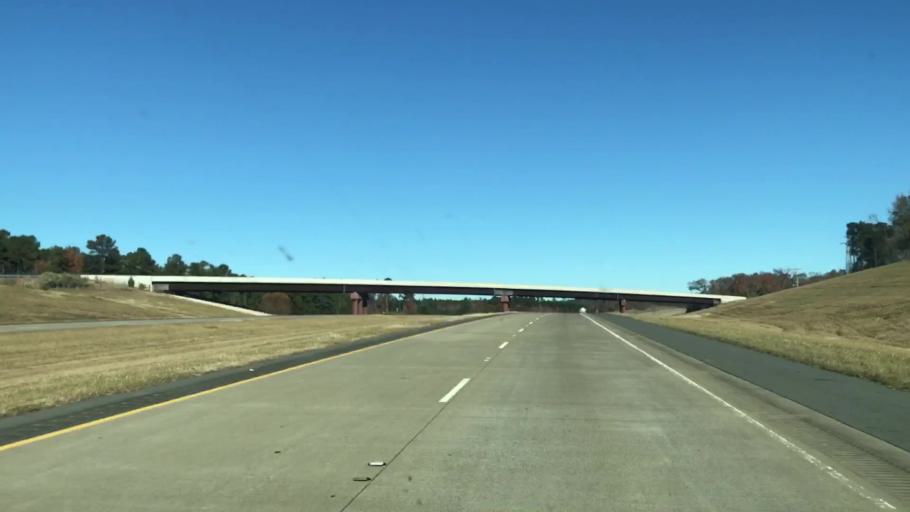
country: US
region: Louisiana
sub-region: Caddo Parish
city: Vivian
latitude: 32.9764
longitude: -93.9090
